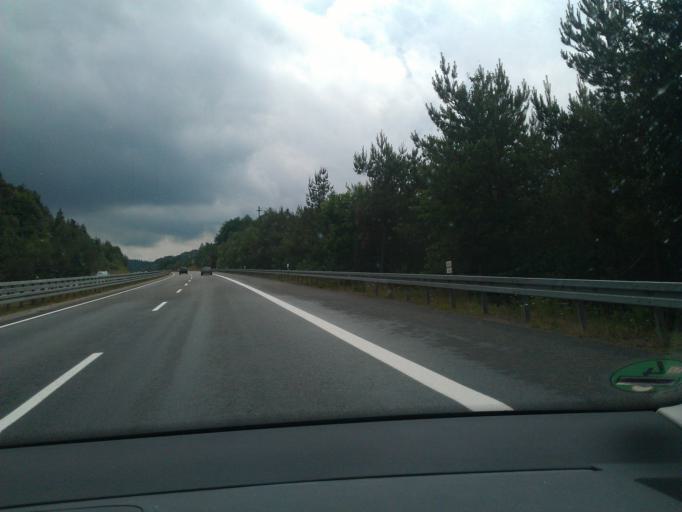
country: DE
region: Saarland
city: Nohfelden
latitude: 49.5985
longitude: 7.1367
